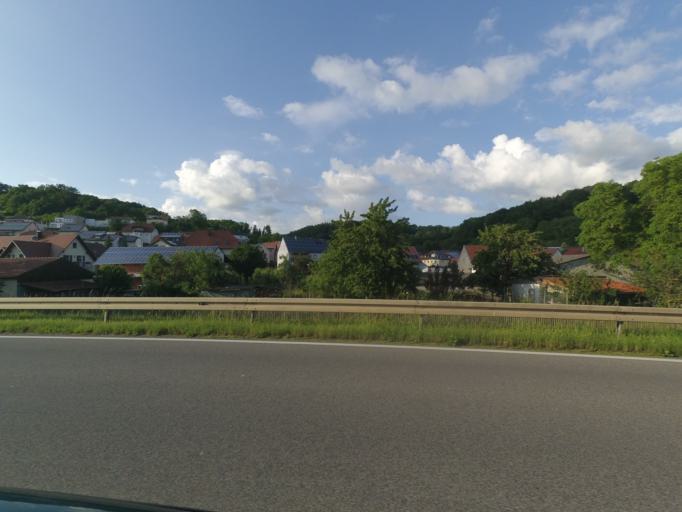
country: DE
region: Bavaria
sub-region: Regierungsbezirk Unterfranken
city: Eltmann
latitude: 49.9932
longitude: 10.6412
